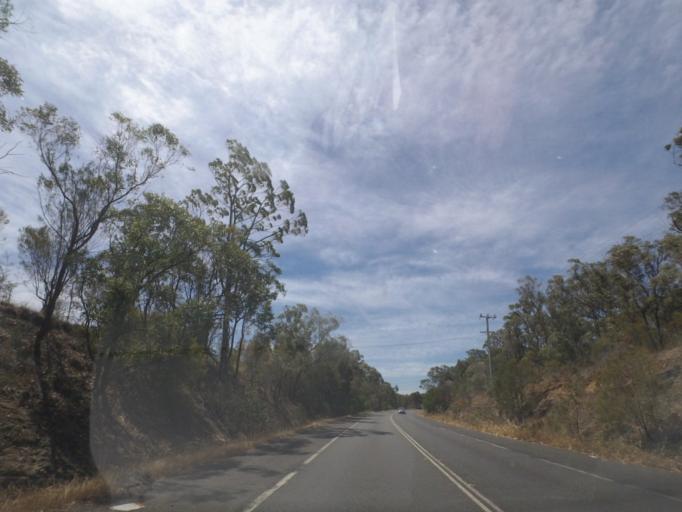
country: AU
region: New South Wales
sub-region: Wollondilly
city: Buxton
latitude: -34.2645
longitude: 150.5730
